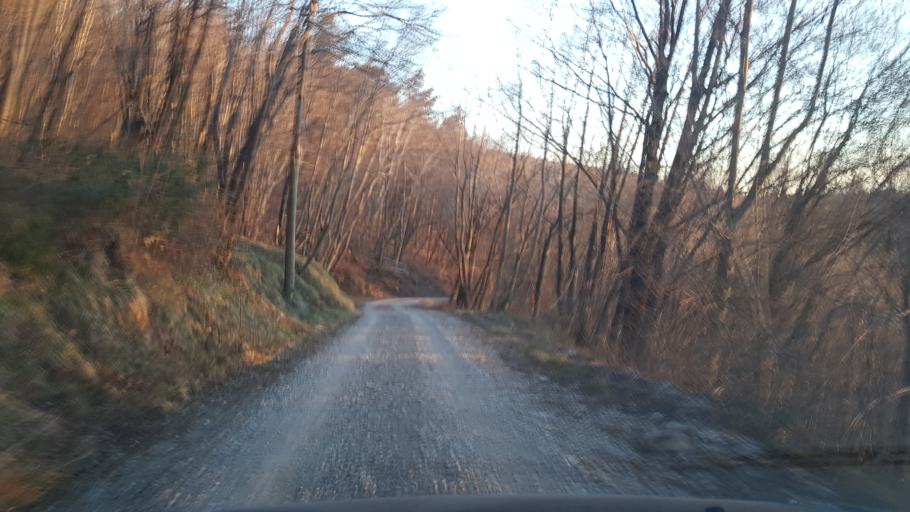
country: SI
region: Nova Gorica
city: Kromberk
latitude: 46.0125
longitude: 13.6989
